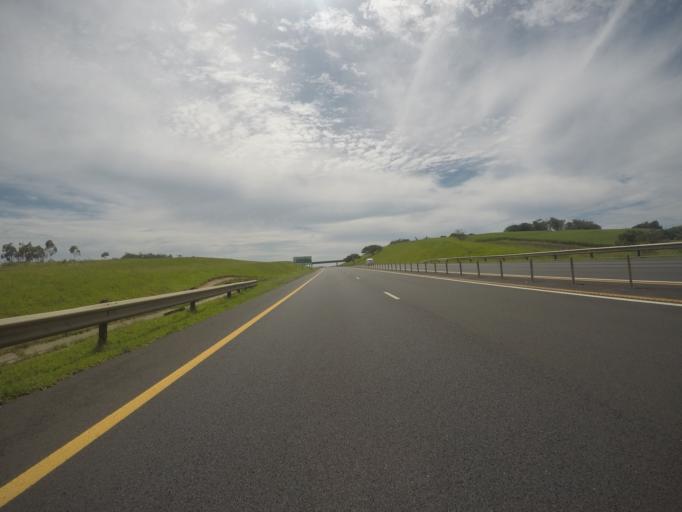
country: ZA
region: KwaZulu-Natal
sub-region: iLembe District Municipality
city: Mandeni
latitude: -29.1777
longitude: 31.5042
